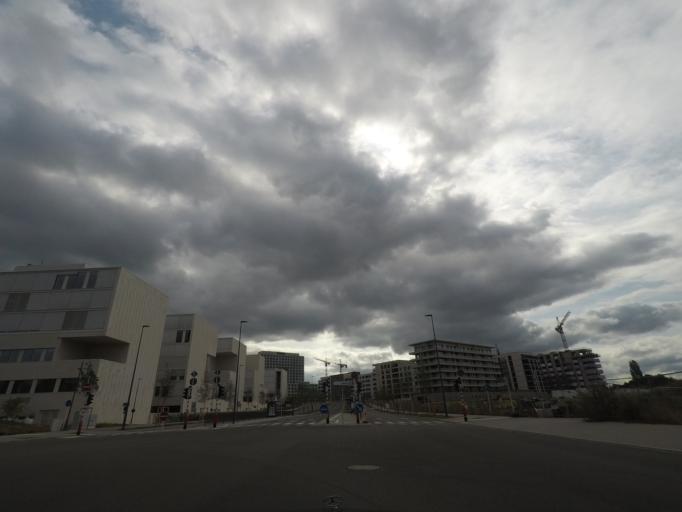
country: LU
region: Luxembourg
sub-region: Canton de Luxembourg
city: Luxembourg
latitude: 49.5851
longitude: 6.1287
